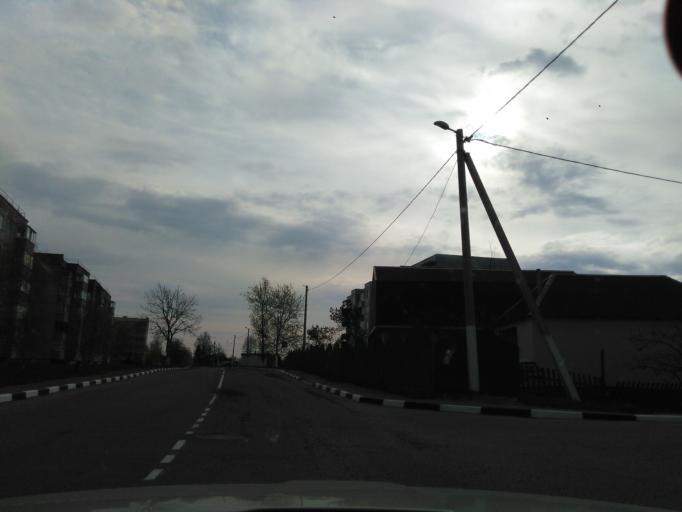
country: BY
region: Vitebsk
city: Chashniki
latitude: 54.8512
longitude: 29.1674
